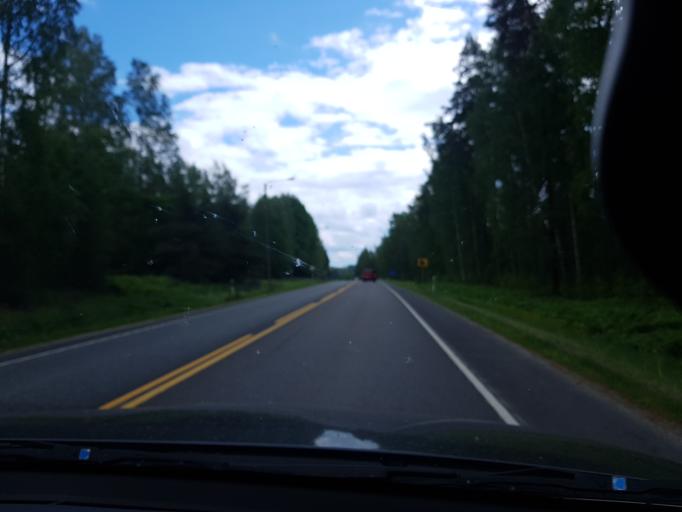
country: FI
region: Pirkanmaa
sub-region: Tampere
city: Paelkaene
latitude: 61.2979
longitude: 24.3078
